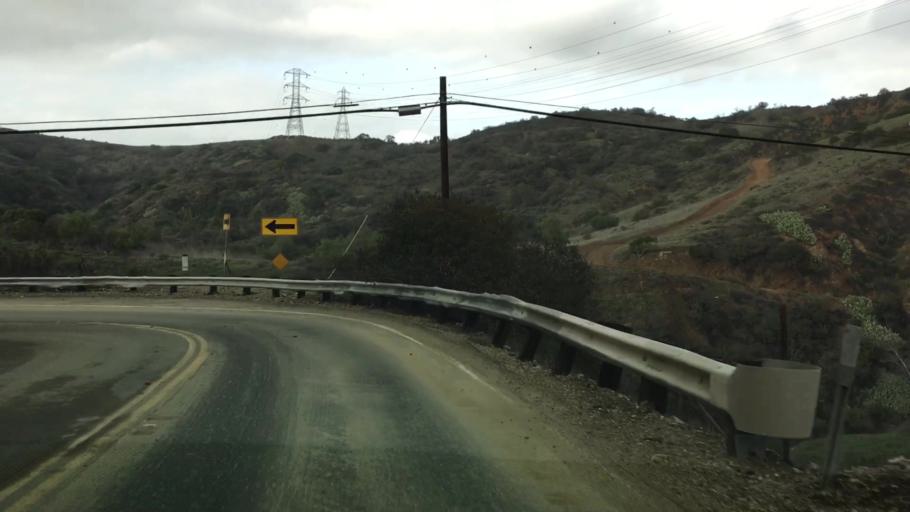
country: US
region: California
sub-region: Los Angeles County
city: Whittier
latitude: 33.9946
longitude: -118.0076
